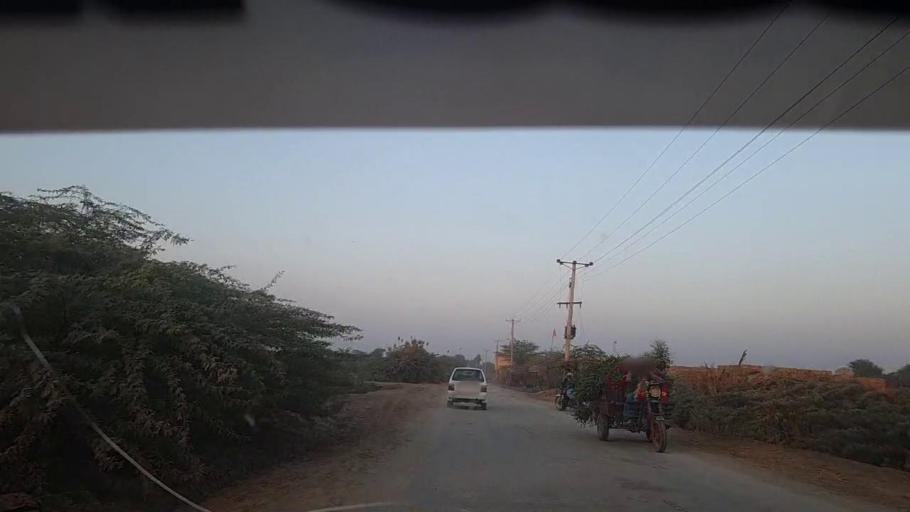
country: PK
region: Sindh
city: Ranipur
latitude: 27.2762
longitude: 68.5141
